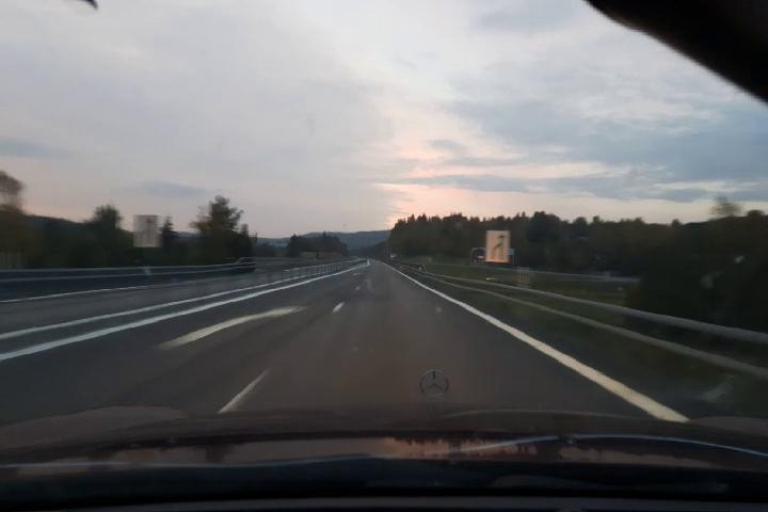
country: SE
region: Vaesternorrland
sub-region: Kramfors Kommun
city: Nordingra
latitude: 62.9281
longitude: 18.0977
